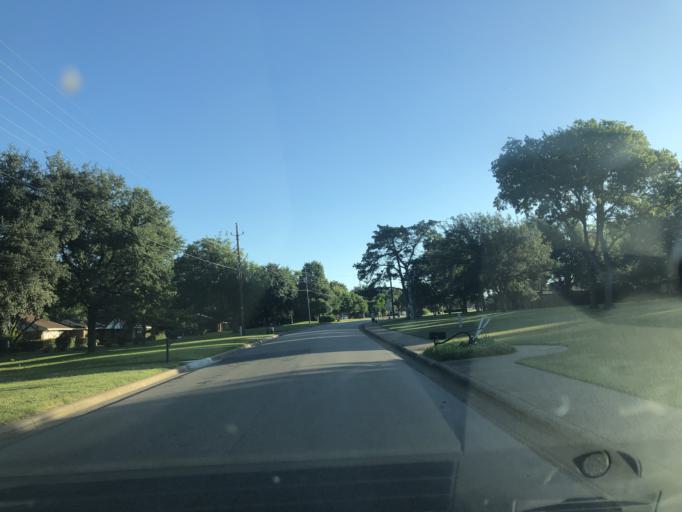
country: US
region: Texas
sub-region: Dallas County
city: Duncanville
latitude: 32.6391
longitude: -96.9351
